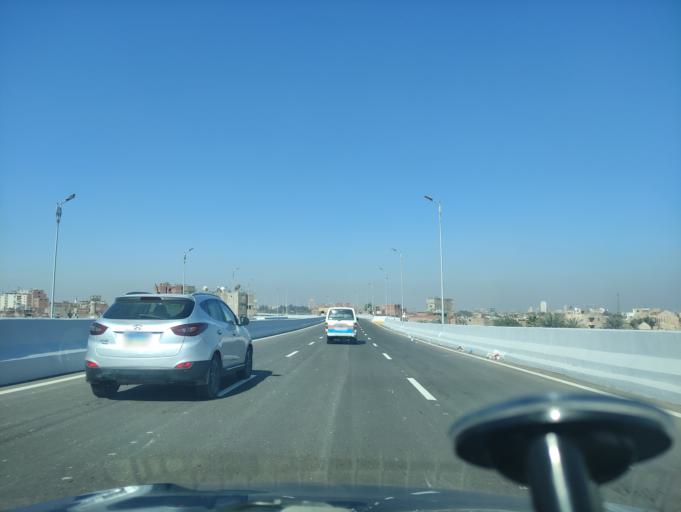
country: EG
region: Al Jizah
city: Al Jizah
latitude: 30.0078
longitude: 31.2603
